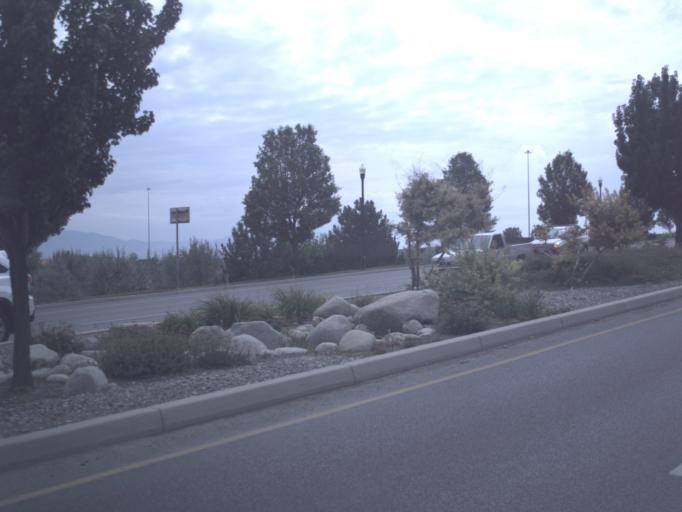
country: US
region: Utah
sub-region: Utah County
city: Pleasant Grove
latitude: 40.3518
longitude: -111.7666
